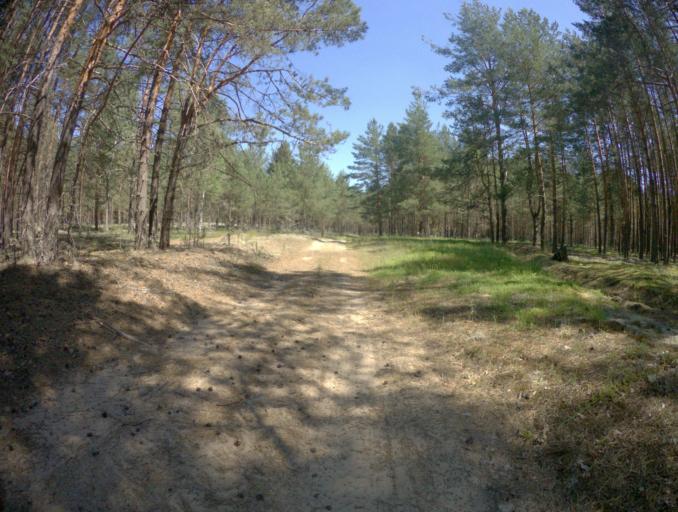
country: RU
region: Ivanovo
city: Talitsy
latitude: 56.3712
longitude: 42.3341
